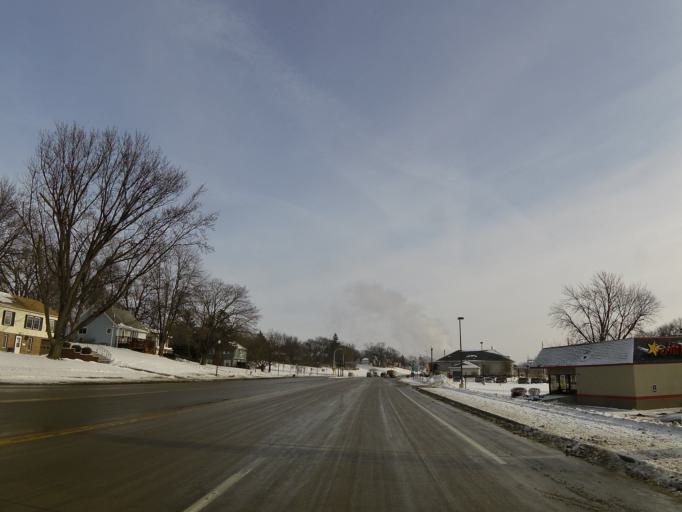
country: US
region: Minnesota
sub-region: McLeod County
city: Hutchinson
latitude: 44.8970
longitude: -94.3724
